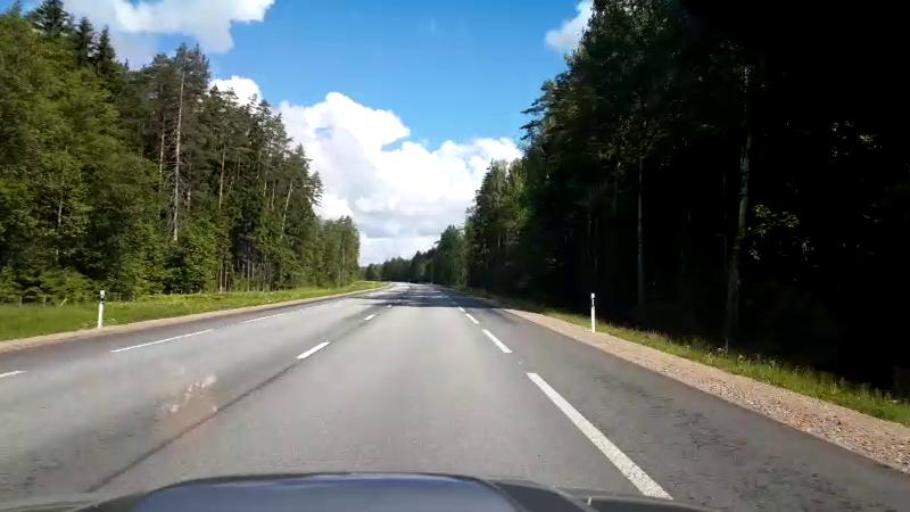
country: LV
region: Kekava
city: Kekava
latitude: 56.7303
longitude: 24.2545
